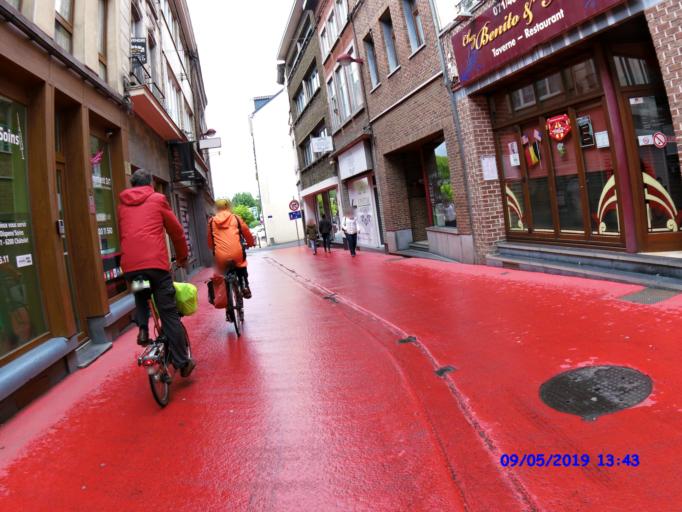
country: BE
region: Wallonia
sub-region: Province du Hainaut
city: Chatelet
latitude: 50.4052
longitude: 4.5222
